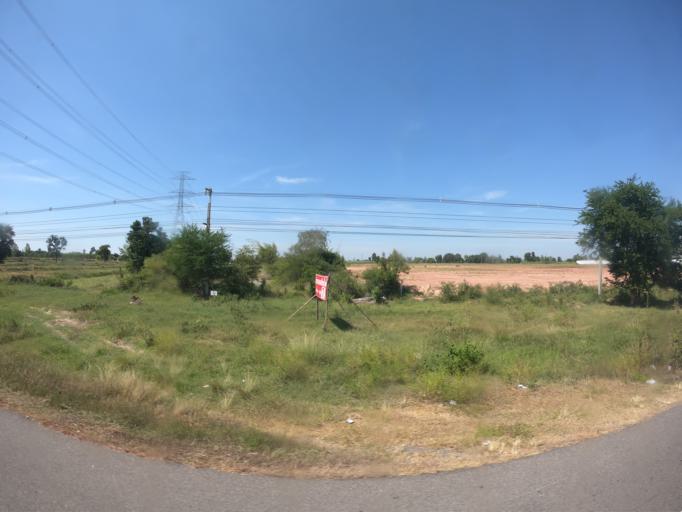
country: TH
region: Khon Kaen
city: Non Sila
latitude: 15.9416
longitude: 102.6772
